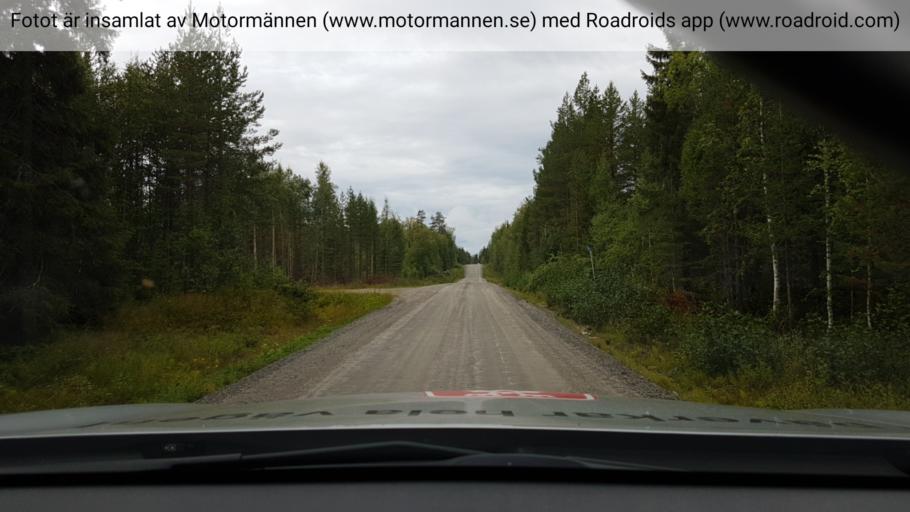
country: SE
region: Vaesterbotten
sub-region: Skelleftea Kommun
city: Langsele
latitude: 64.6900
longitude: 20.1685
